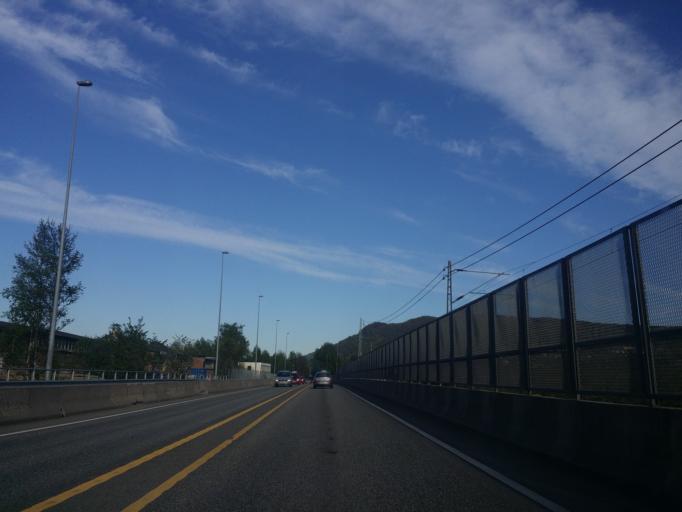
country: NO
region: Buskerud
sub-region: Nedre Eiker
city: Mjondalen
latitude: 59.7533
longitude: 9.9950
